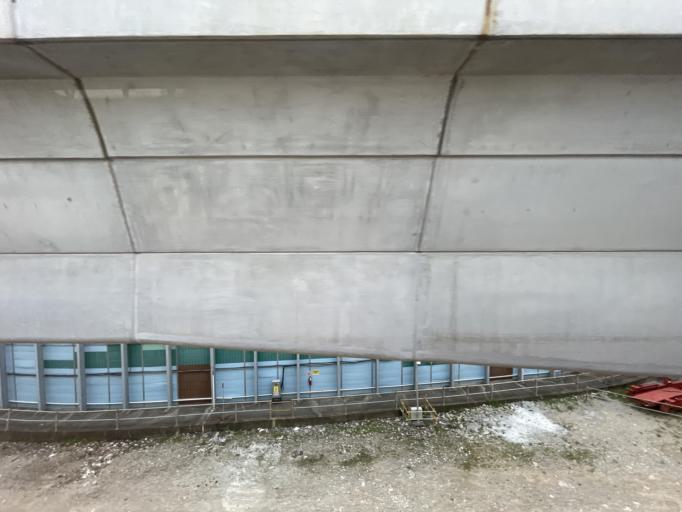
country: SG
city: Singapore
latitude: 1.3351
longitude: 103.9564
